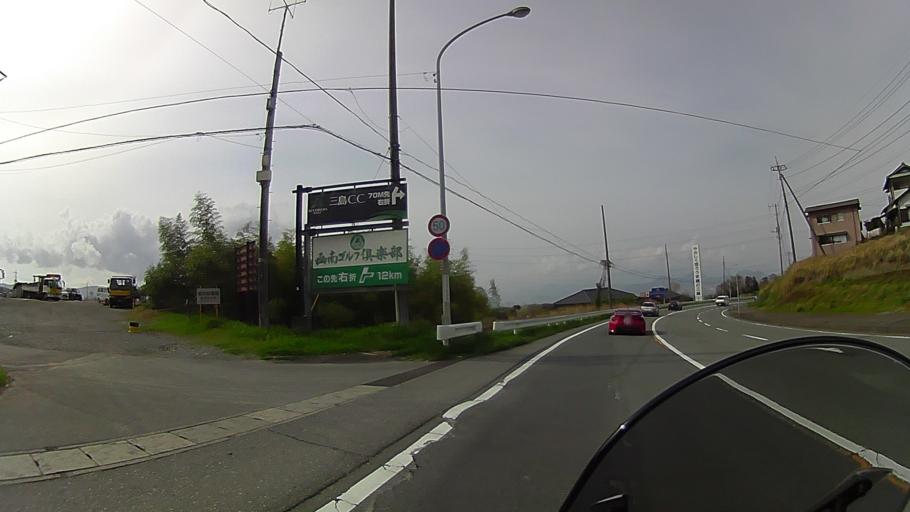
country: JP
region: Shizuoka
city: Mishima
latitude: 35.1425
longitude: 138.9770
